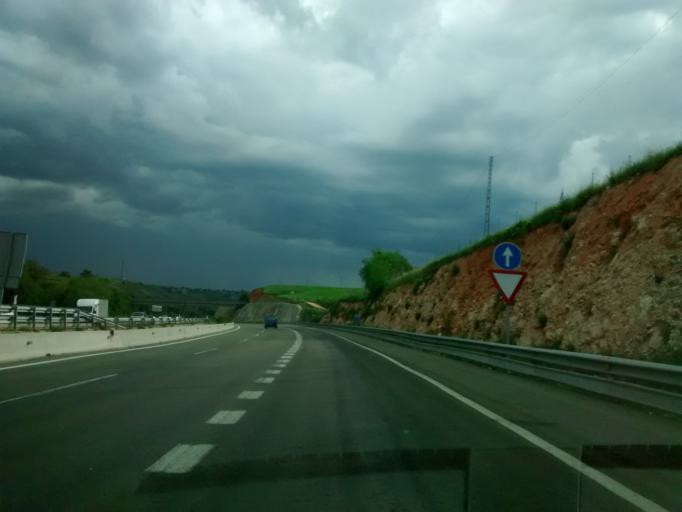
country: ES
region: Castille-La Mancha
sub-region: Provincia de Guadalajara
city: Torija
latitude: 40.7458
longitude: -3.0334
